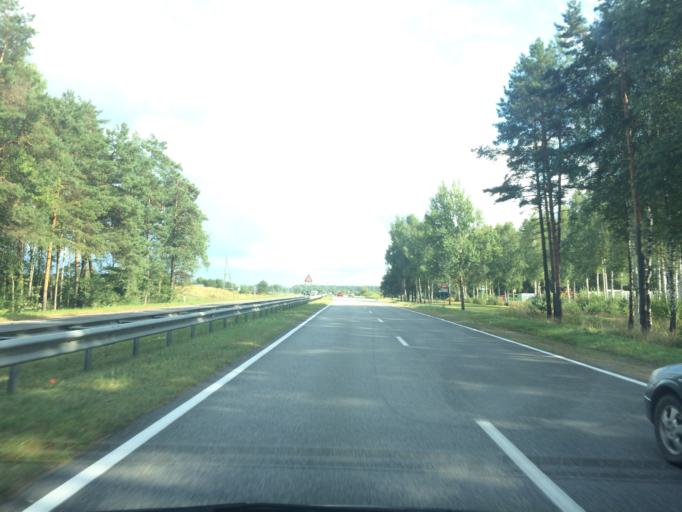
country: LV
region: Ikskile
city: Ikskile
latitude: 56.8244
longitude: 24.5303
